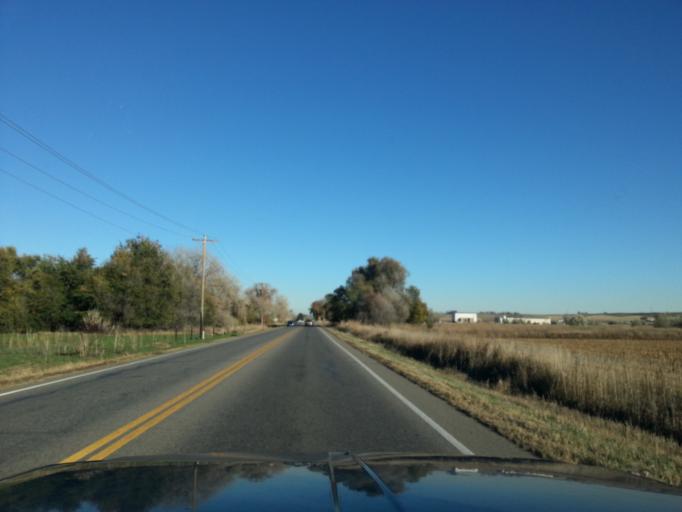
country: US
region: Colorado
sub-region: Larimer County
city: Loveland
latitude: 40.3783
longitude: -105.0609
